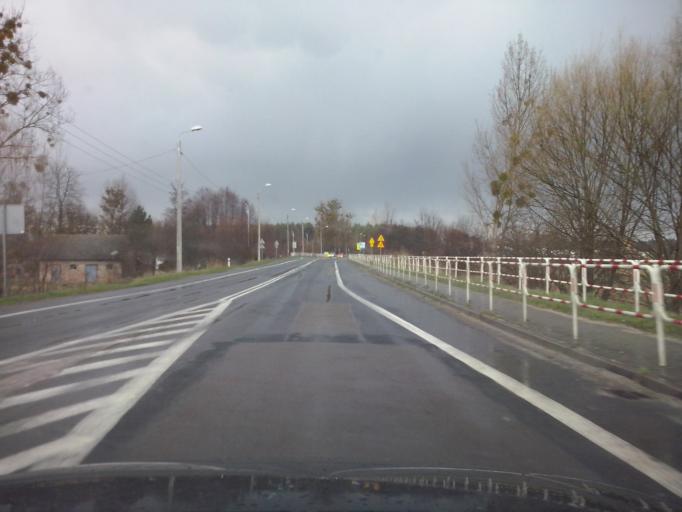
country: PL
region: Lublin Voivodeship
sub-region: Powiat krasnostawski
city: Krasnystaw
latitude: 51.0134
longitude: 23.1918
